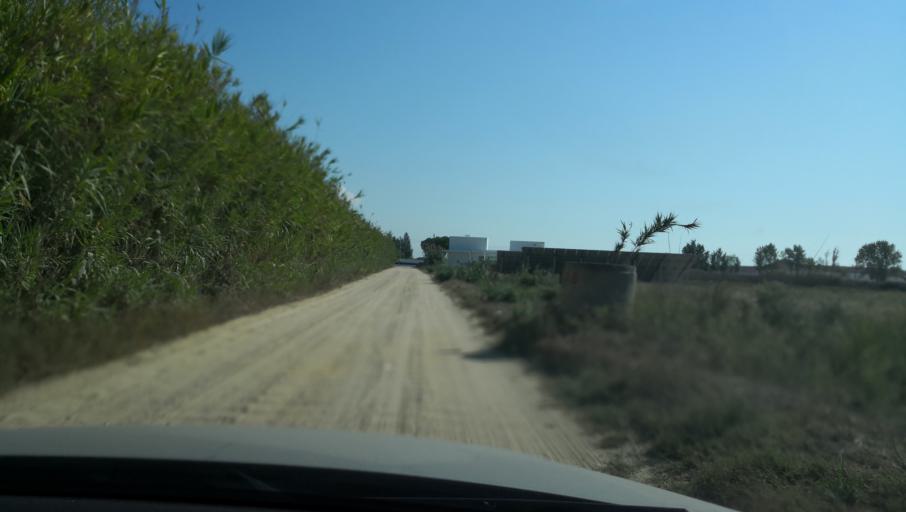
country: PT
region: Setubal
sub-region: Setubal
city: Setubal
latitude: 38.3832
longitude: -8.7887
